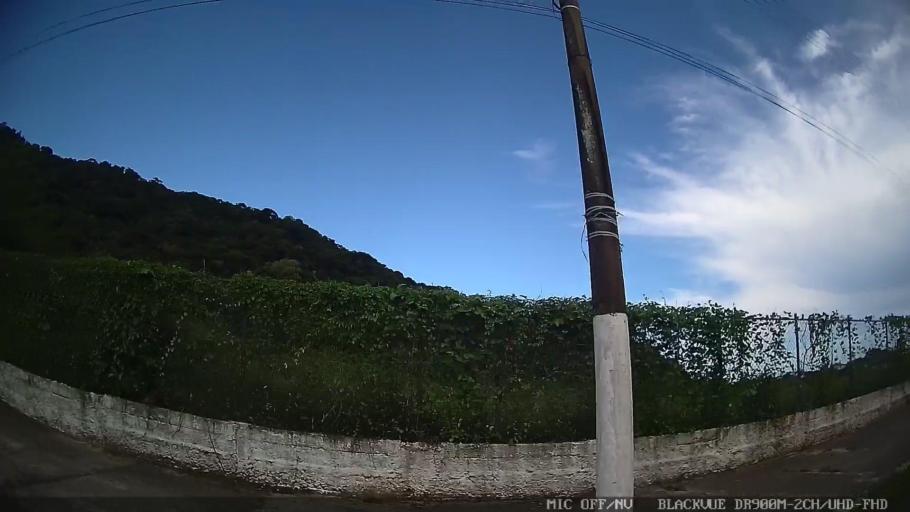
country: BR
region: Sao Paulo
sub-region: Iguape
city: Iguape
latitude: -24.7014
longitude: -47.5530
